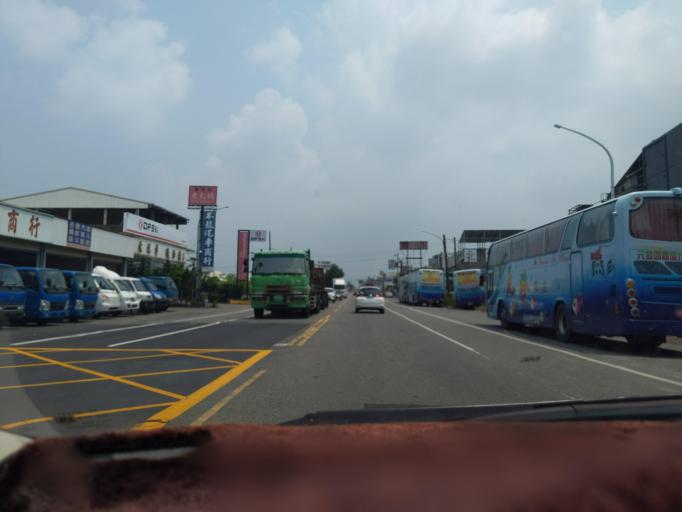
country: TW
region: Taiwan
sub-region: Yunlin
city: Douliu
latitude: 23.7931
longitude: 120.4689
